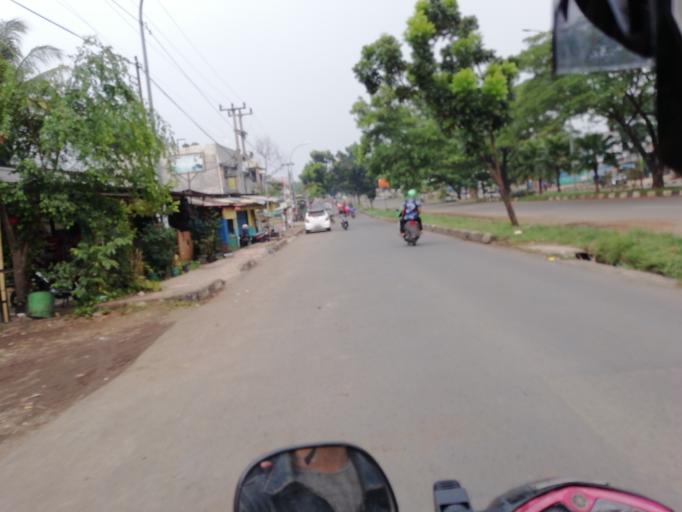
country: ID
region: West Java
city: Cibinong
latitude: -6.4800
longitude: 106.8049
